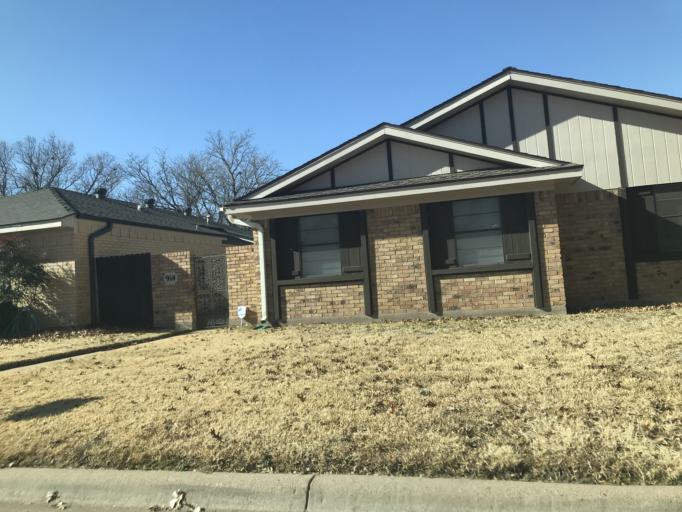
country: US
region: Texas
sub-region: Taylor County
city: Abilene
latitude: 32.4590
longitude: -99.7019
